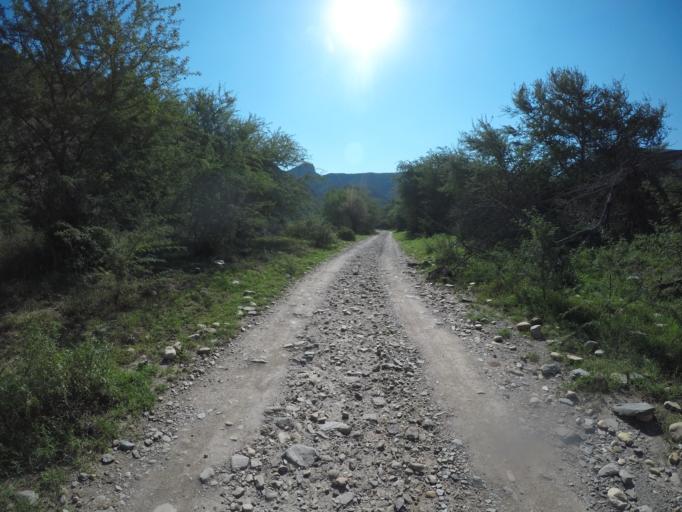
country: ZA
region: Eastern Cape
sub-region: Cacadu District Municipality
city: Kareedouw
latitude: -33.6596
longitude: 24.3666
